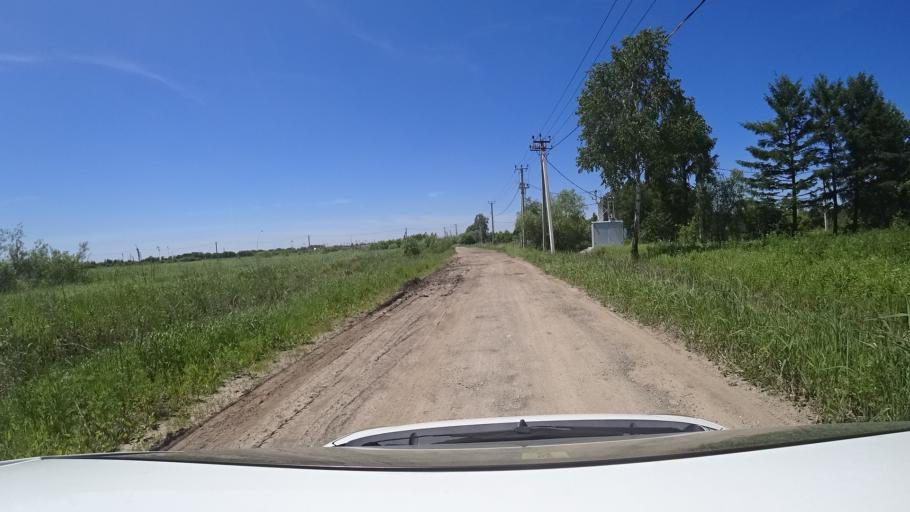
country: RU
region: Khabarovsk Krai
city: Topolevo
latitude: 48.5004
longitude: 135.1968
